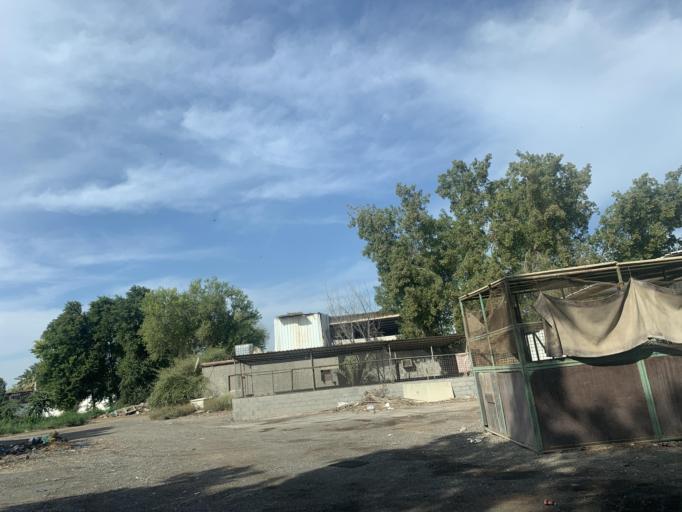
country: BH
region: Central Governorate
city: Madinat Hamad
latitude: 26.1251
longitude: 50.4732
